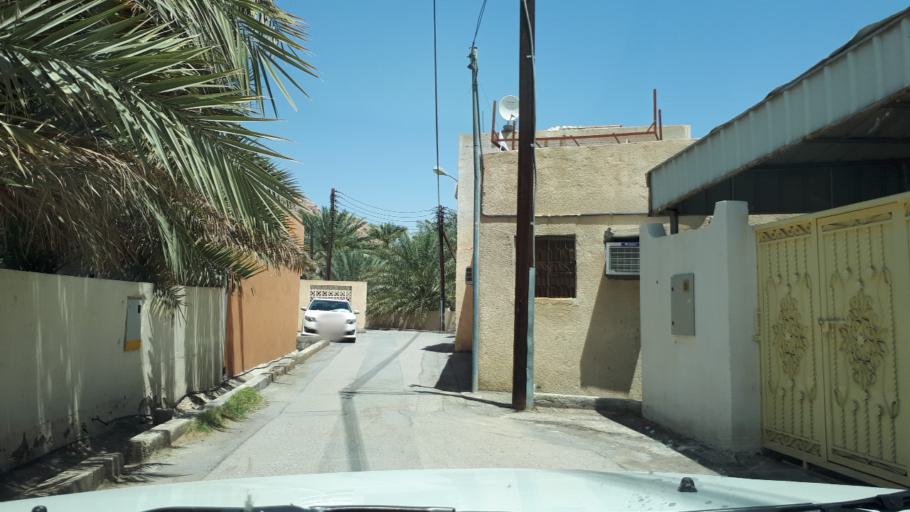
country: OM
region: Muhafazat ad Dakhiliyah
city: Nizwa
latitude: 22.8826
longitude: 57.5276
